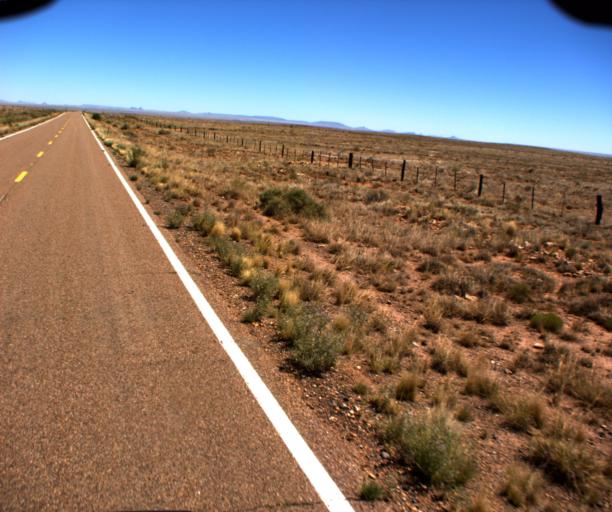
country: US
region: Arizona
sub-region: Navajo County
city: Winslow
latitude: 34.8888
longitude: -110.6486
